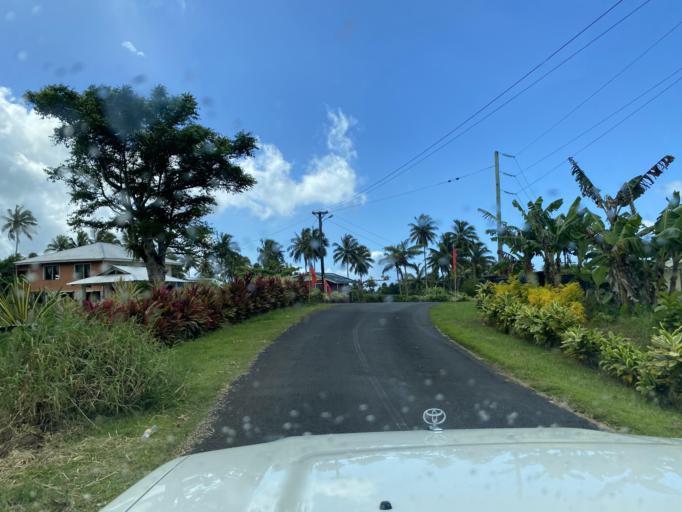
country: WS
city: Matavai
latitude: -13.9894
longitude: -171.5863
